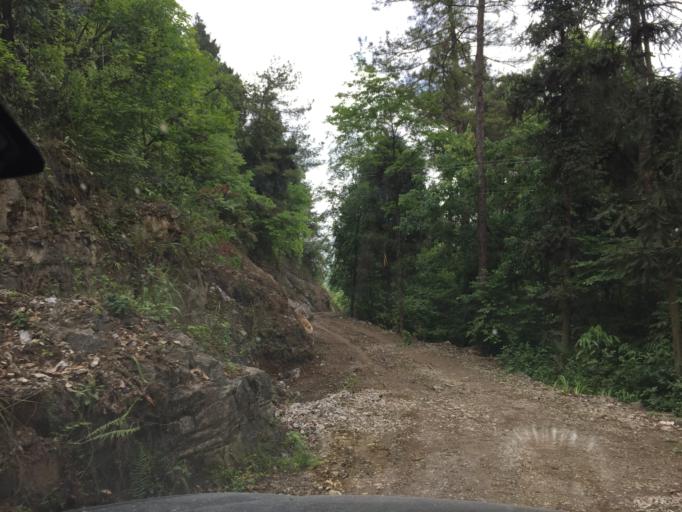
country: CN
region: Guizhou Sheng
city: Kuanping
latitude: 28.0163
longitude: 108.0691
